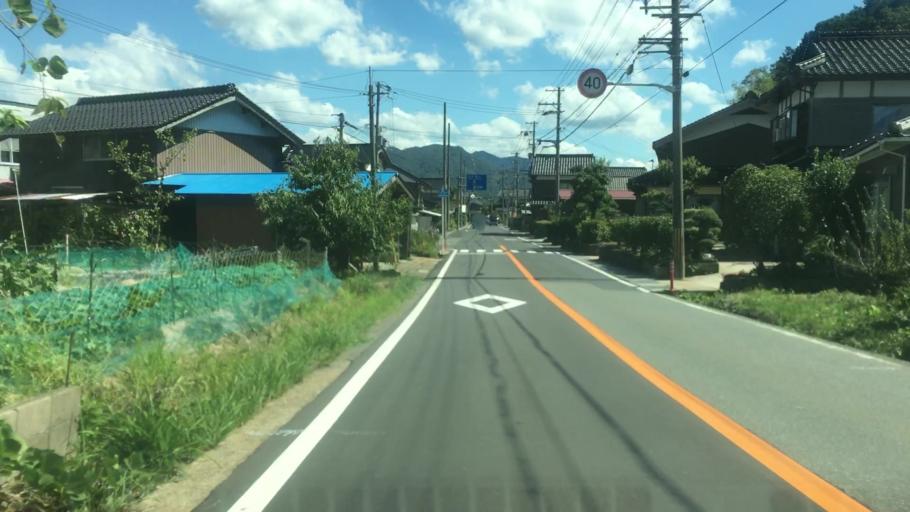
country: JP
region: Hyogo
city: Toyooka
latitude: 35.5905
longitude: 134.9238
